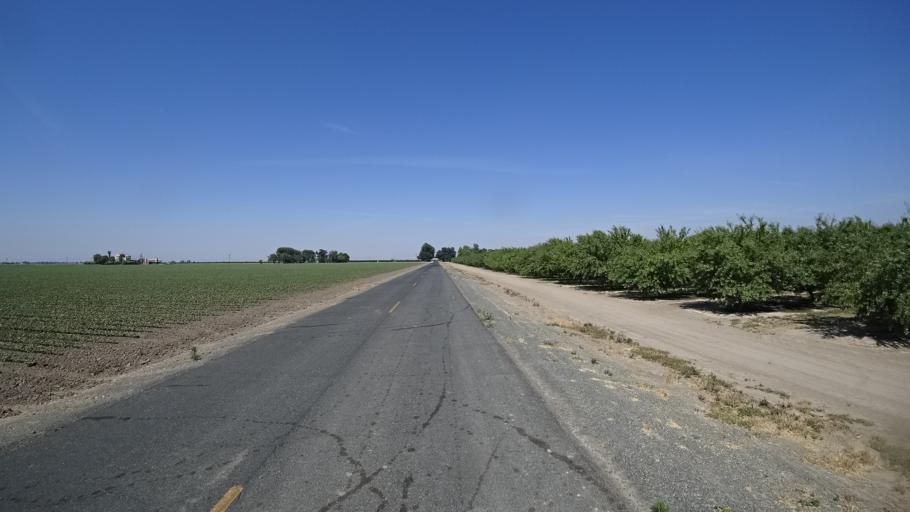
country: US
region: California
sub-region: Kings County
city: Lemoore
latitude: 36.3279
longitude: -119.8393
